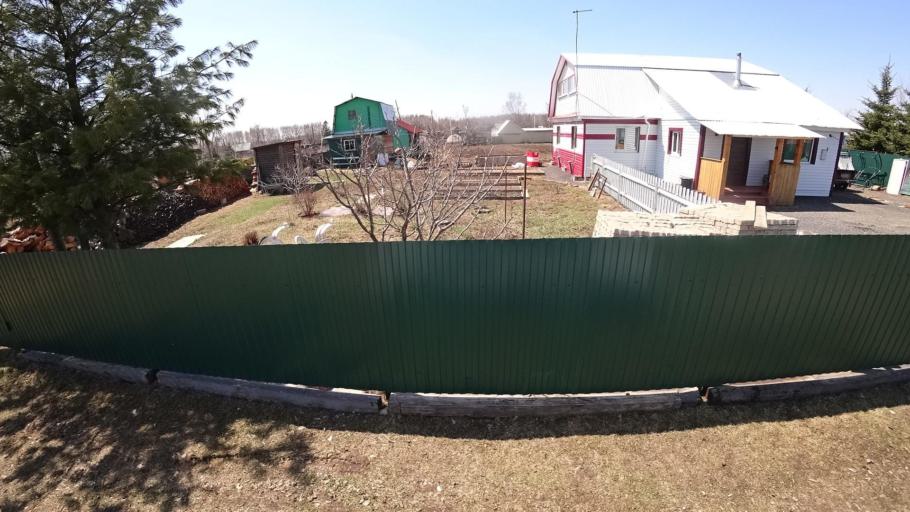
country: RU
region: Khabarovsk Krai
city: Khurba
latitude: 50.4090
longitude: 136.8692
